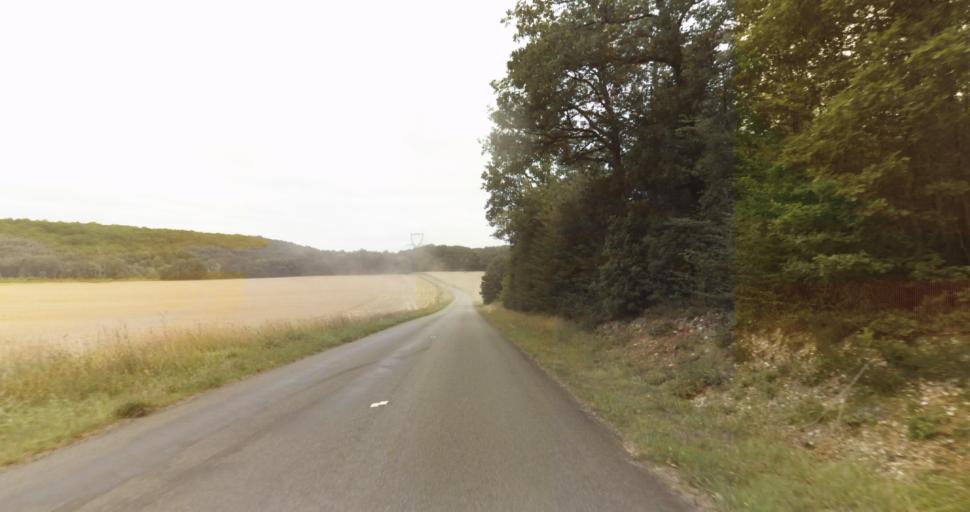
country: FR
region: Haute-Normandie
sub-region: Departement de l'Eure
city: La Couture-Boussey
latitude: 48.8848
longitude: 1.3782
